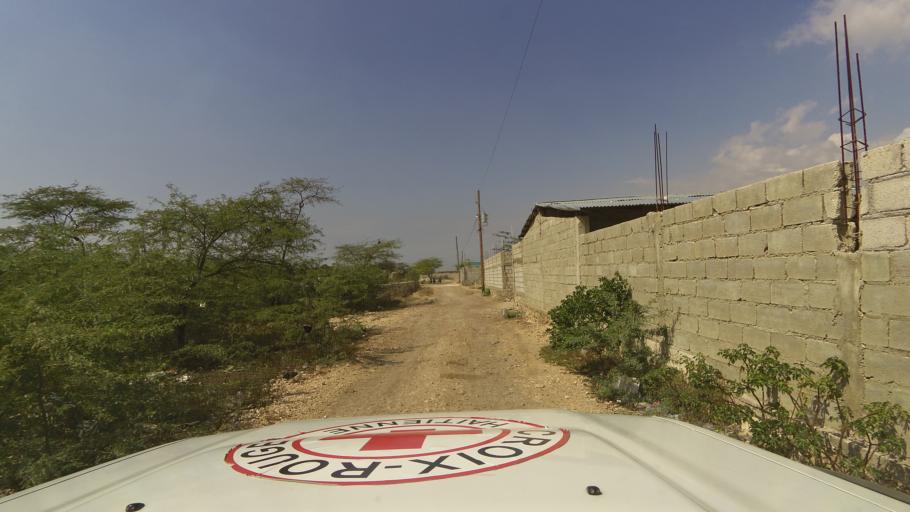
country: HT
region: Ouest
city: Croix des Bouquets
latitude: 18.6421
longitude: -72.2628
